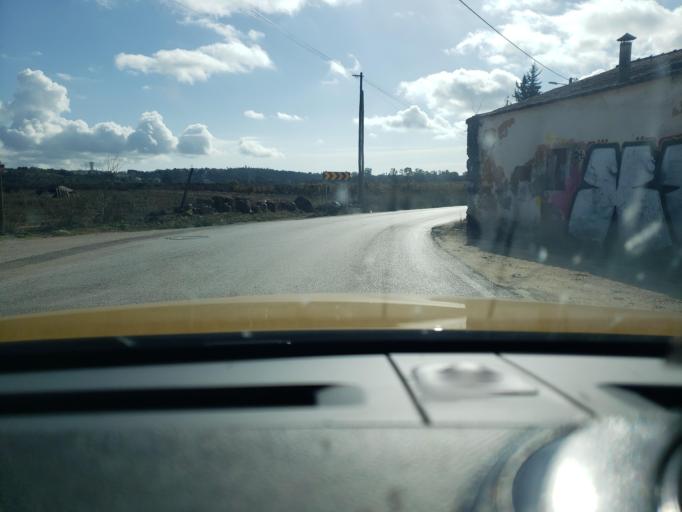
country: PT
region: Faro
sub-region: Portimao
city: Alvor
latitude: 37.1671
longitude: -8.5779
